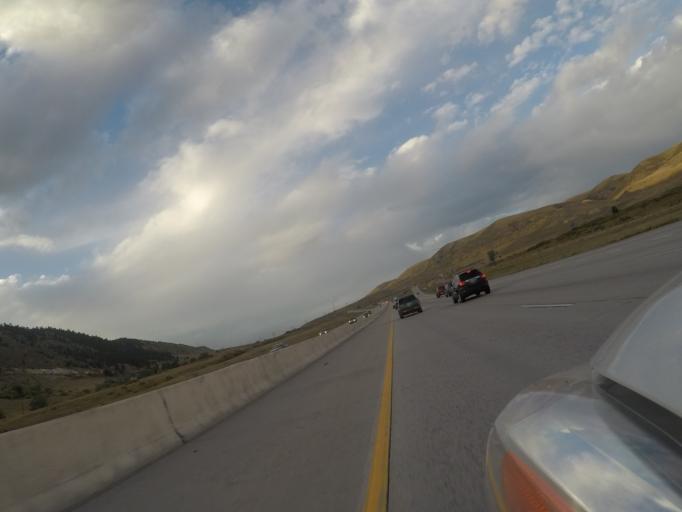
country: US
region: Colorado
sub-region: Jefferson County
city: West Pleasant View
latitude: 39.6798
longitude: -105.1887
